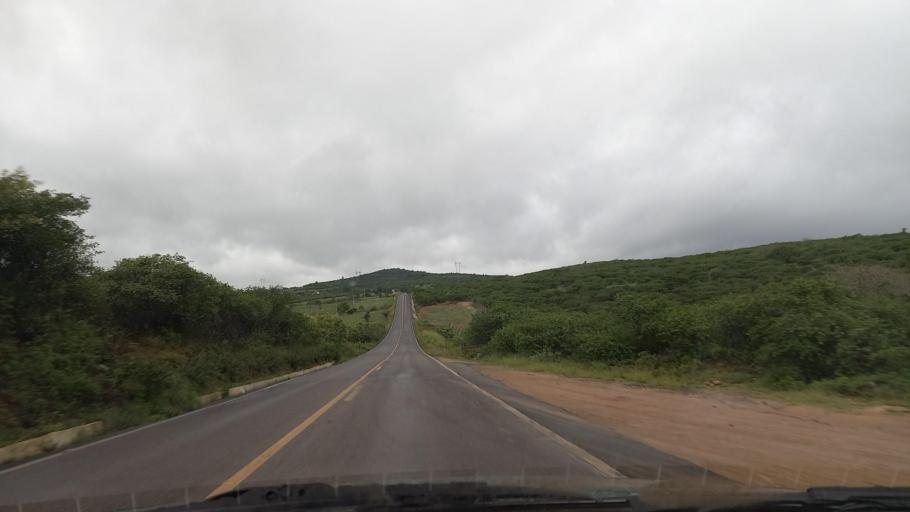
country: BR
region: Pernambuco
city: Garanhuns
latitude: -8.8416
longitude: -36.5309
